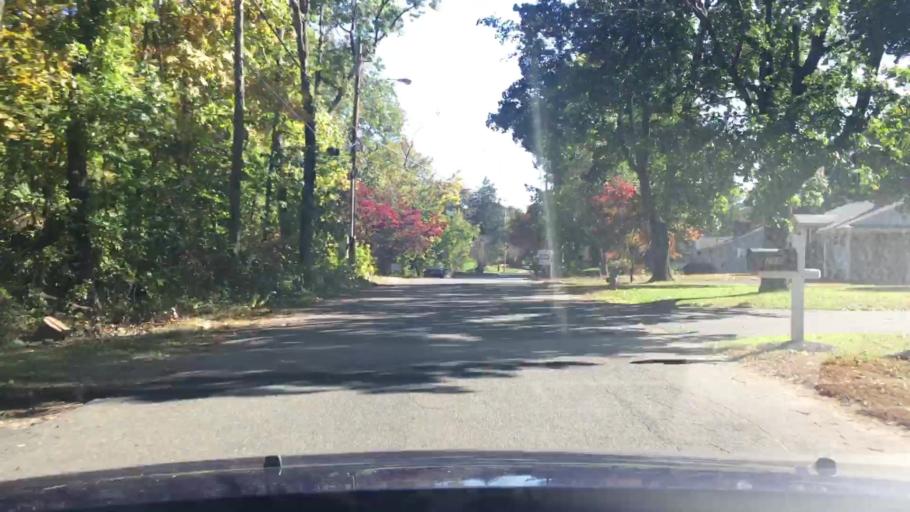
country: US
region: Massachusetts
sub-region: Essex County
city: North Andover
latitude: 42.6835
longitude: -71.0991
